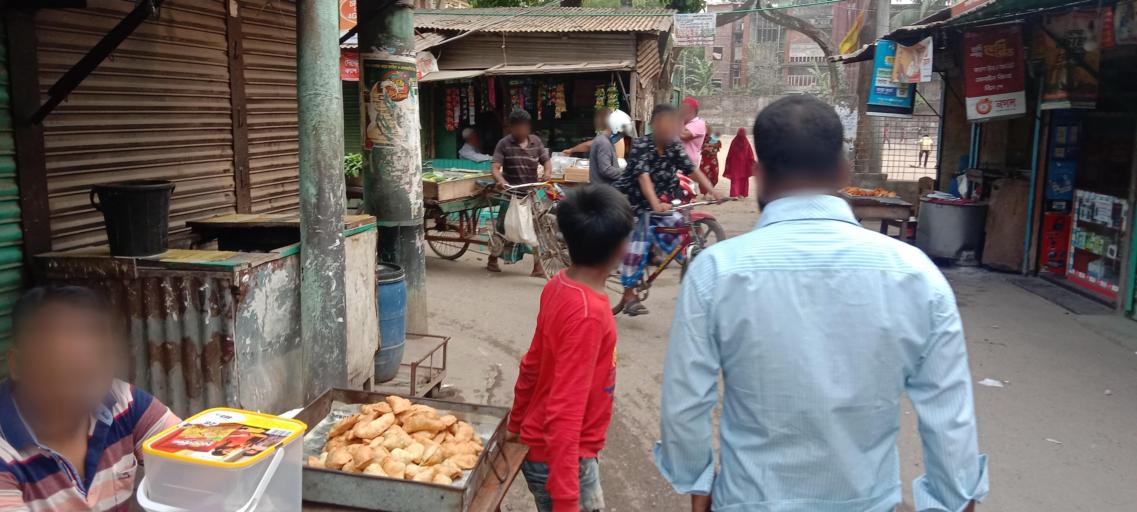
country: BD
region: Dhaka
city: Azimpur
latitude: 23.7059
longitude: 90.3830
